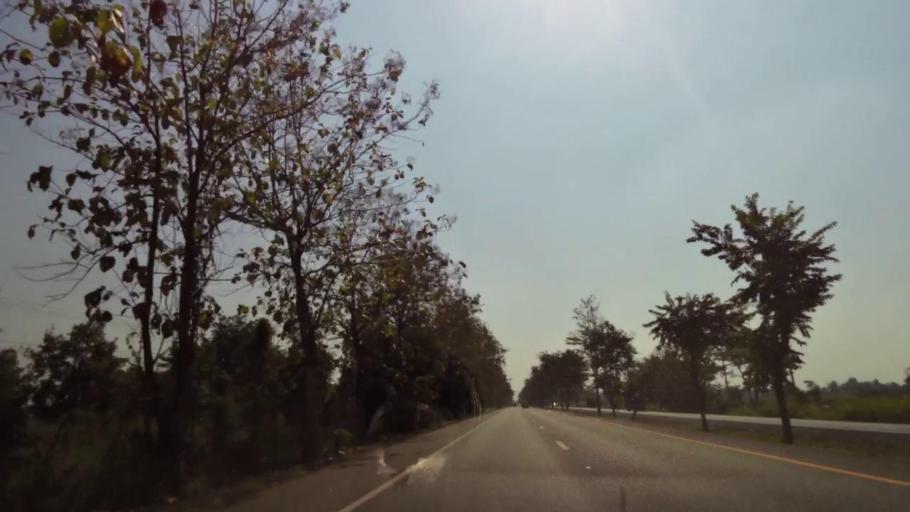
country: TH
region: Phichit
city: Bueng Na Rang
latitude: 16.0855
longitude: 100.1248
